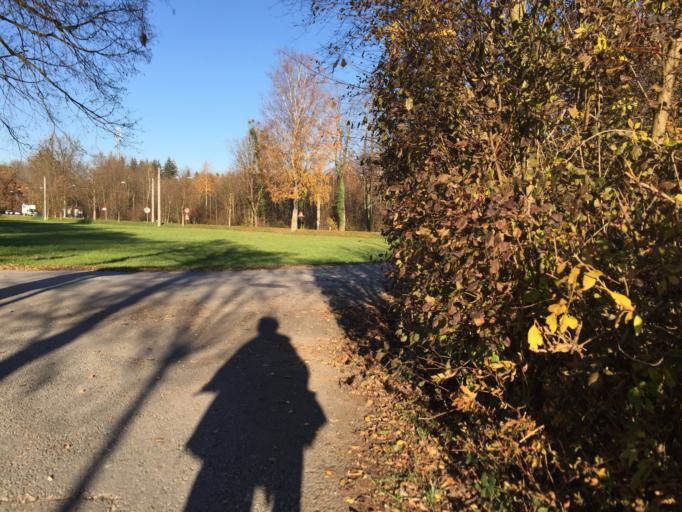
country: AT
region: Salzburg
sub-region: Politischer Bezirk Salzburg-Umgebung
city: Anif
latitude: 47.7640
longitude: 13.0392
